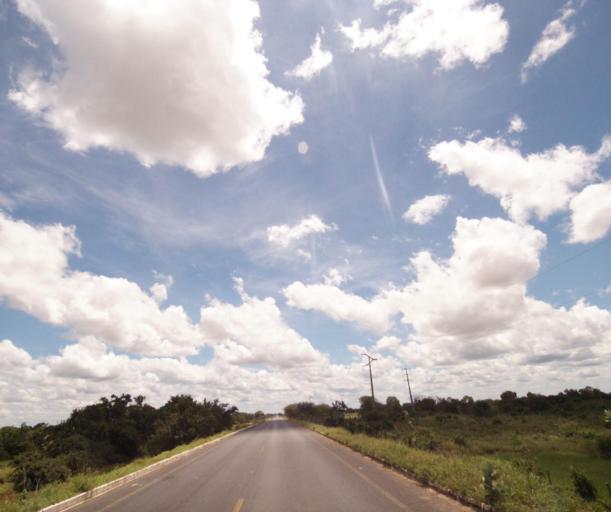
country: BR
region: Bahia
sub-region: Bom Jesus Da Lapa
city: Bom Jesus da Lapa
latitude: -13.2578
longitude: -43.4670
